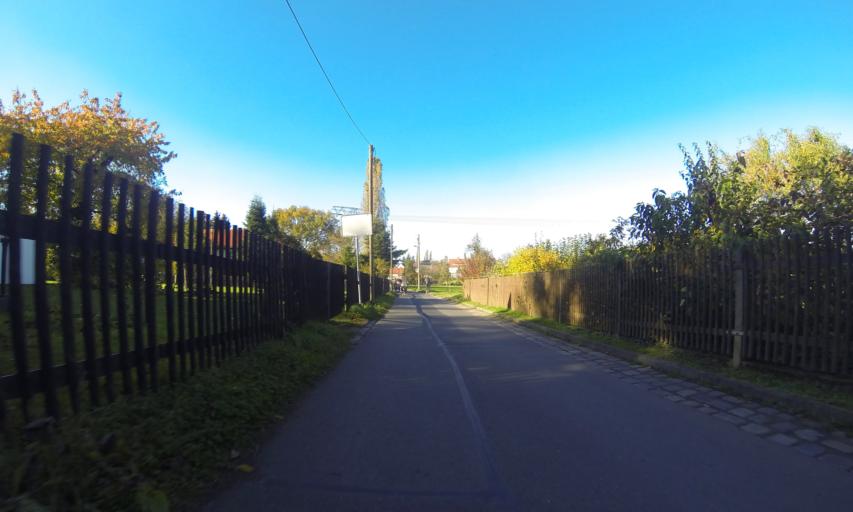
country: DE
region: Saxony
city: Radebeul
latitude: 51.0931
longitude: 13.6601
